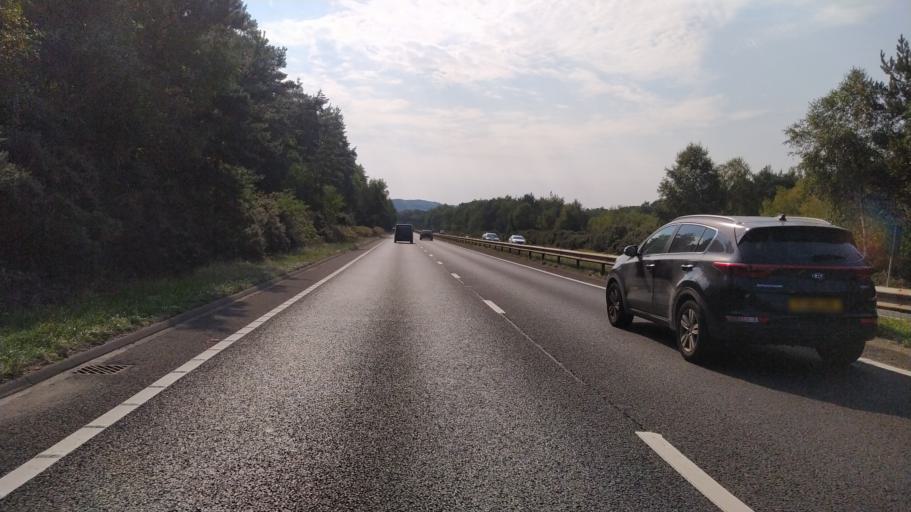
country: GB
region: England
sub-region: Hampshire
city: Liss
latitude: 51.0704
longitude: -0.8810
